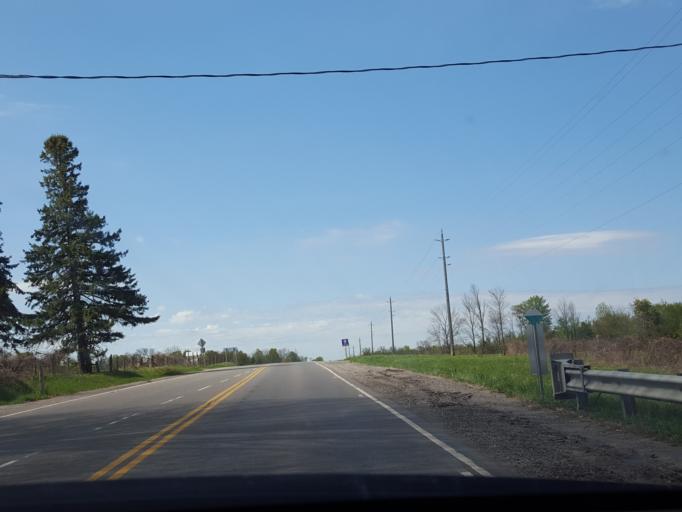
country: CA
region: Ontario
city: Uxbridge
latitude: 44.1535
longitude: -78.9010
